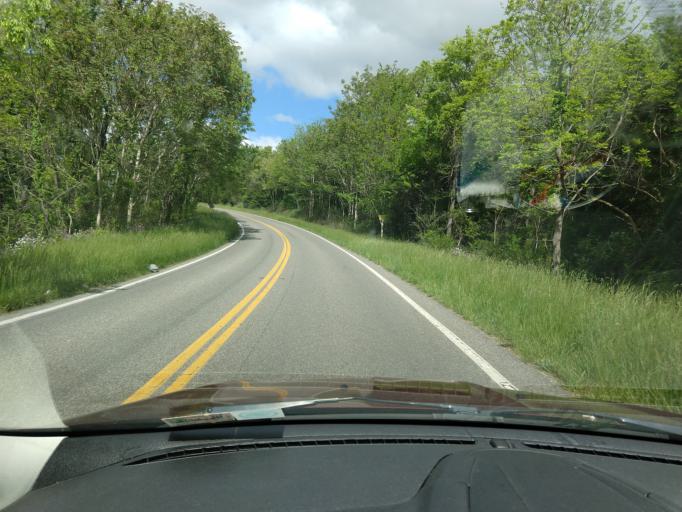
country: US
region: Virginia
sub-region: Wythe County
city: Wytheville
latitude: 36.8384
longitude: -80.9563
